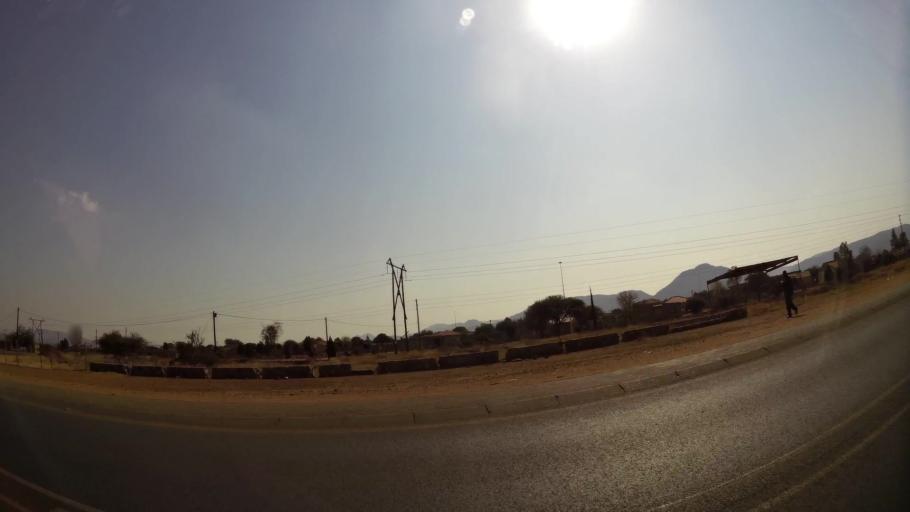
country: ZA
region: North-West
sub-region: Bojanala Platinum District Municipality
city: Mogwase
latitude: -25.3768
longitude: 27.0622
